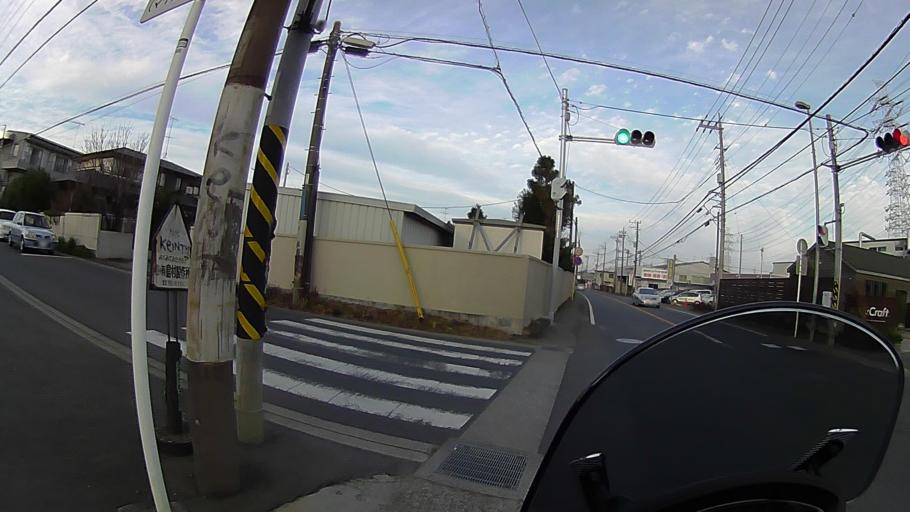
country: JP
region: Kanagawa
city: Minami-rinkan
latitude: 35.4216
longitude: 139.4249
